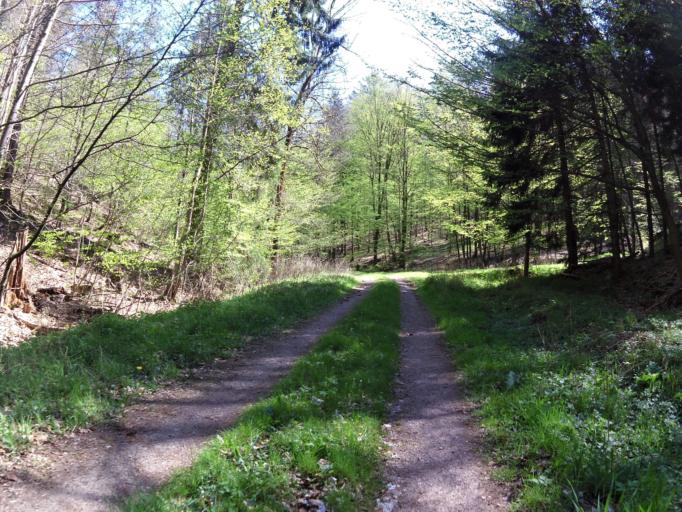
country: DE
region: Thuringia
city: Krauthausen
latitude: 50.9760
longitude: 10.2509
